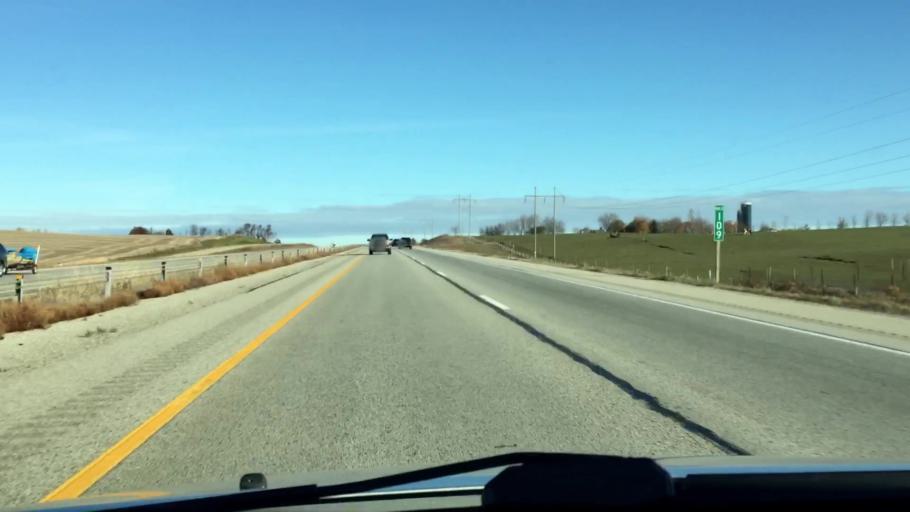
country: US
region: Wisconsin
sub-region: Fond du Lac County
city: Rosendale
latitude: 43.8867
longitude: -88.5837
